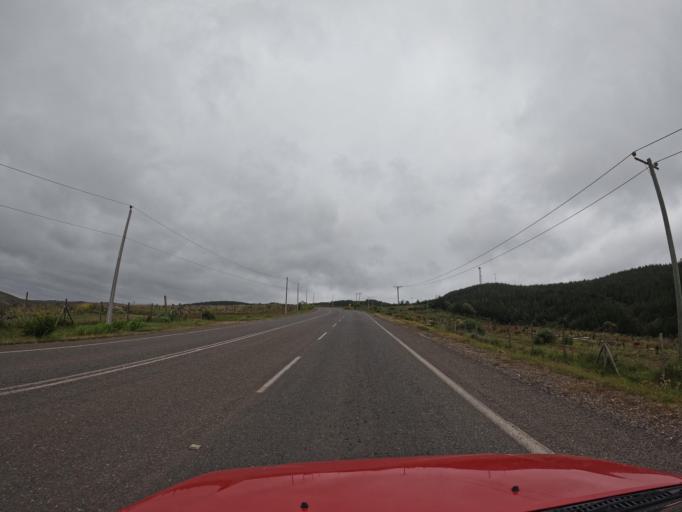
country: CL
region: O'Higgins
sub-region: Provincia de Colchagua
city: Santa Cruz
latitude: -34.6342
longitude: -72.0250
